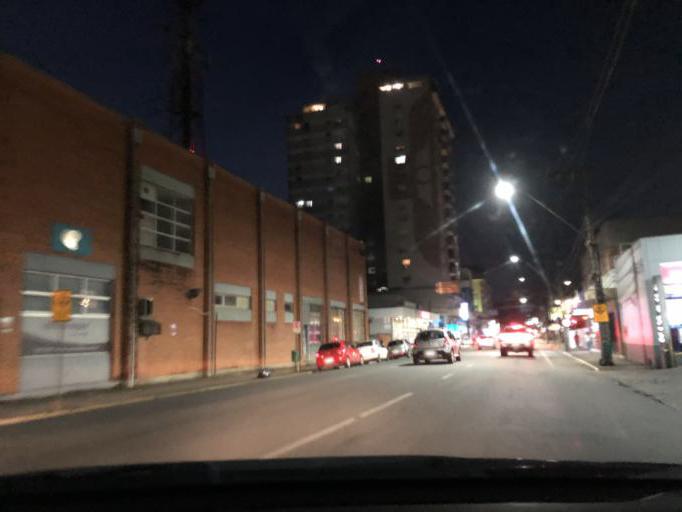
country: BR
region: Santa Catarina
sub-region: Jaragua Do Sul
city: Jaragua do Sul
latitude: -26.4805
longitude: -49.0813
